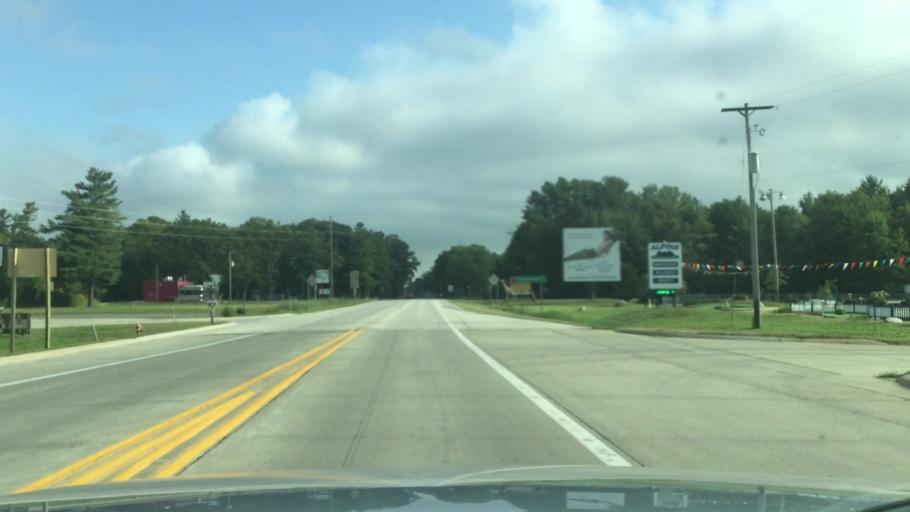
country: US
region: Michigan
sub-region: Saginaw County
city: Birch Run
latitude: 43.2516
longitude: -83.7354
